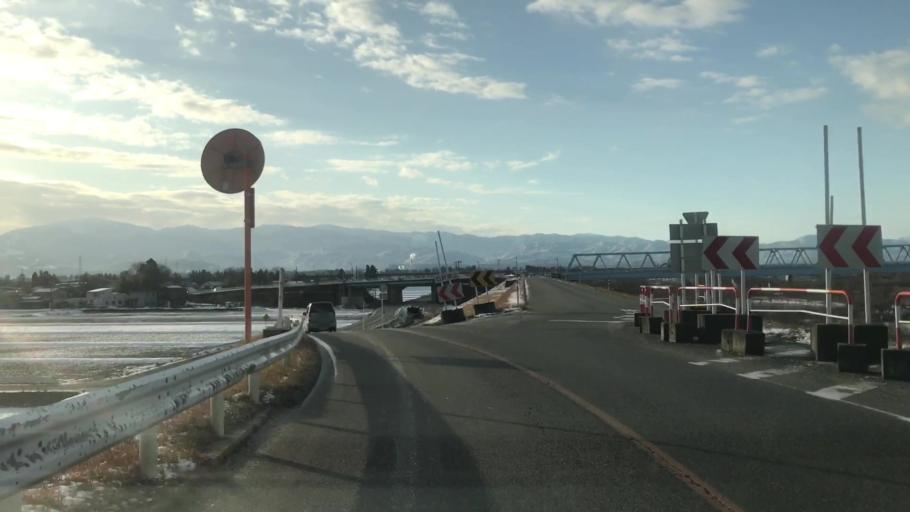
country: JP
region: Toyama
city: Toyama-shi
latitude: 36.6749
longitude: 137.2856
